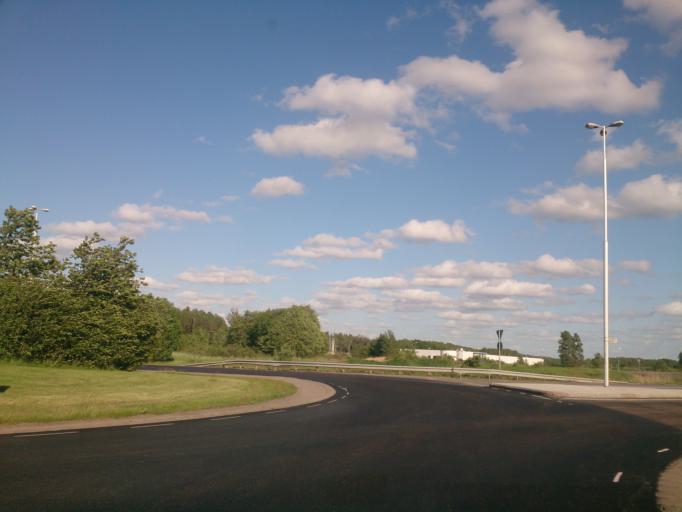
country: SE
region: OEstergoetland
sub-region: Linkopings Kommun
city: Linkoping
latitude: 58.3892
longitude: 15.5806
